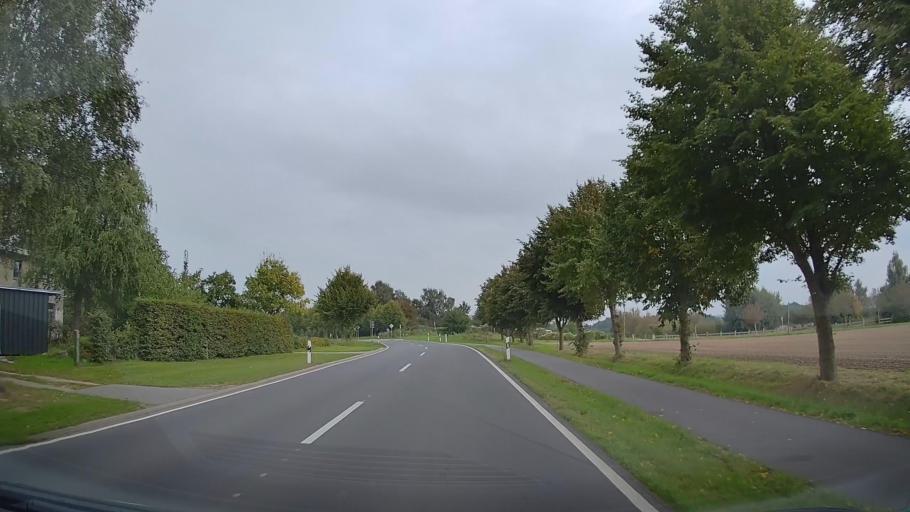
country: DE
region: Mecklenburg-Vorpommern
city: Ostseebad Kuhlungsborn
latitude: 54.1322
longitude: 11.7704
